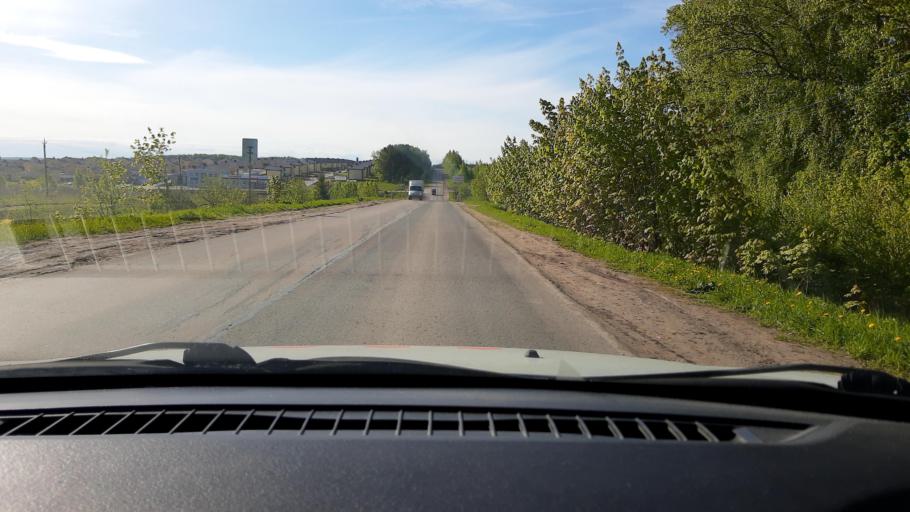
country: RU
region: Nizjnij Novgorod
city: Burevestnik
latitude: 56.1700
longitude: 43.7645
